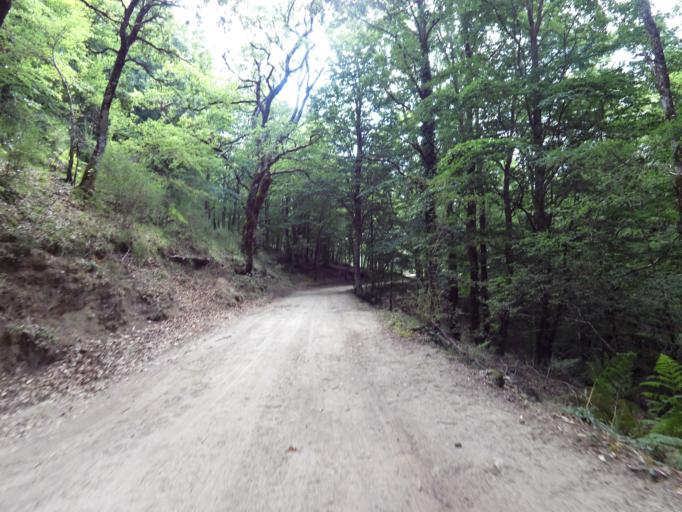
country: IT
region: Calabria
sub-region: Provincia di Vibo-Valentia
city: Nardodipace
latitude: 38.5096
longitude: 16.3824
